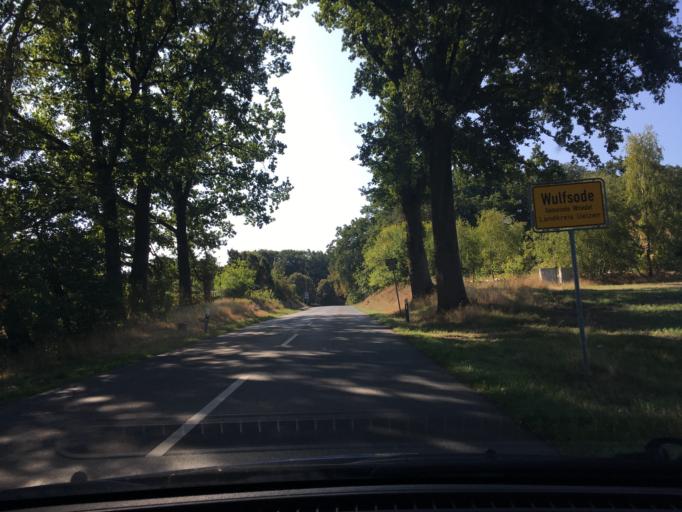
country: DE
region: Lower Saxony
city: Rehlingen
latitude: 53.0649
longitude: 10.2342
